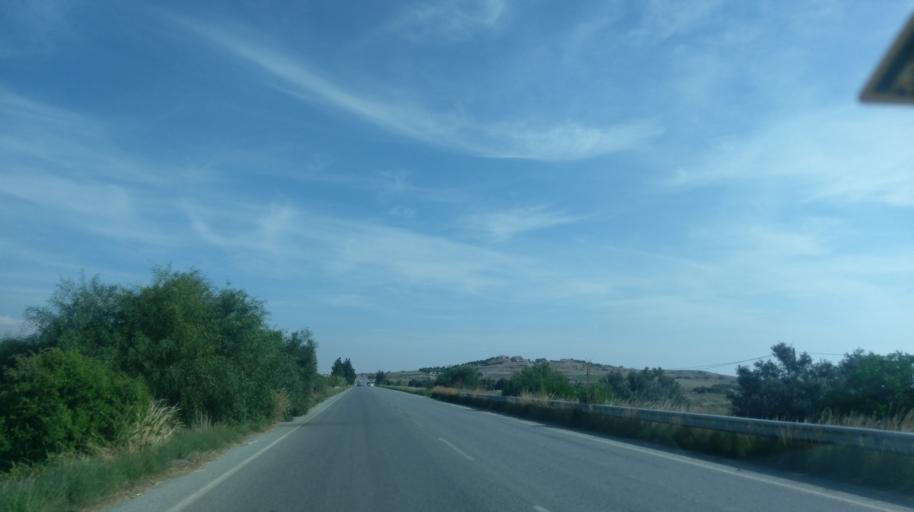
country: CY
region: Ammochostos
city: Lefkonoiko
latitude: 35.2504
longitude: 33.6199
